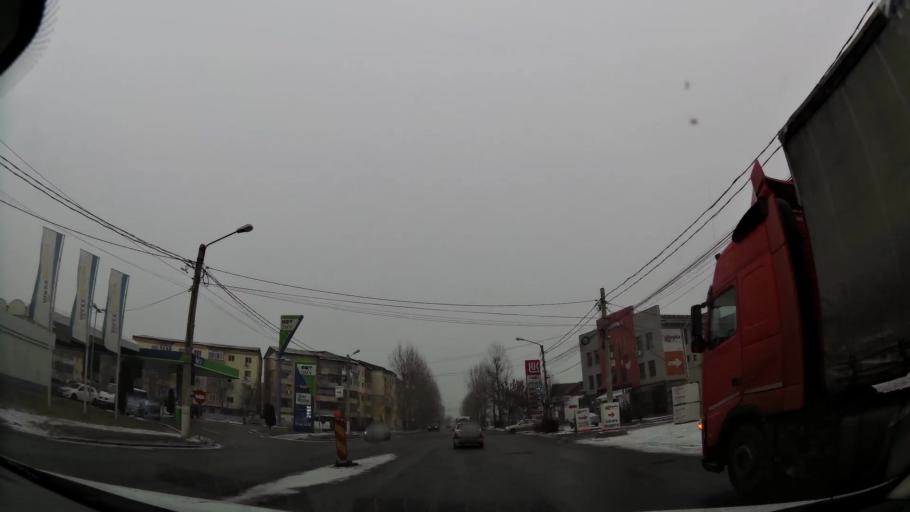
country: RO
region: Dambovita
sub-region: Municipiul Targoviste
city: Targoviste
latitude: 44.9120
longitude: 25.4745
